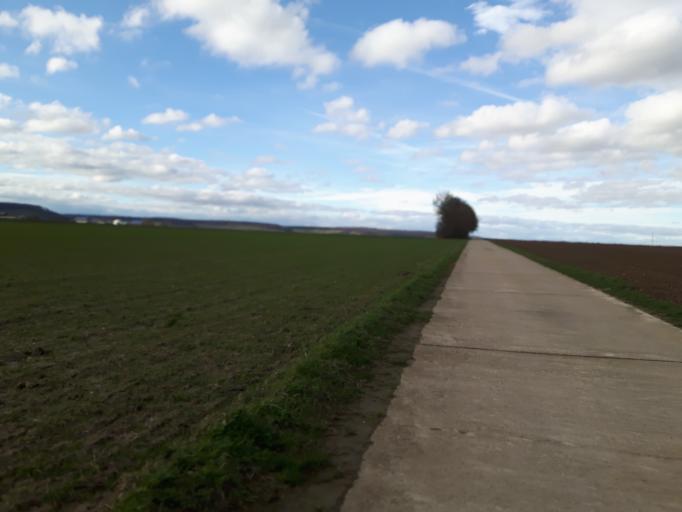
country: DE
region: Baden-Wuerttemberg
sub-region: Regierungsbezirk Stuttgart
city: Nordheim
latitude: 49.0857
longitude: 9.1165
